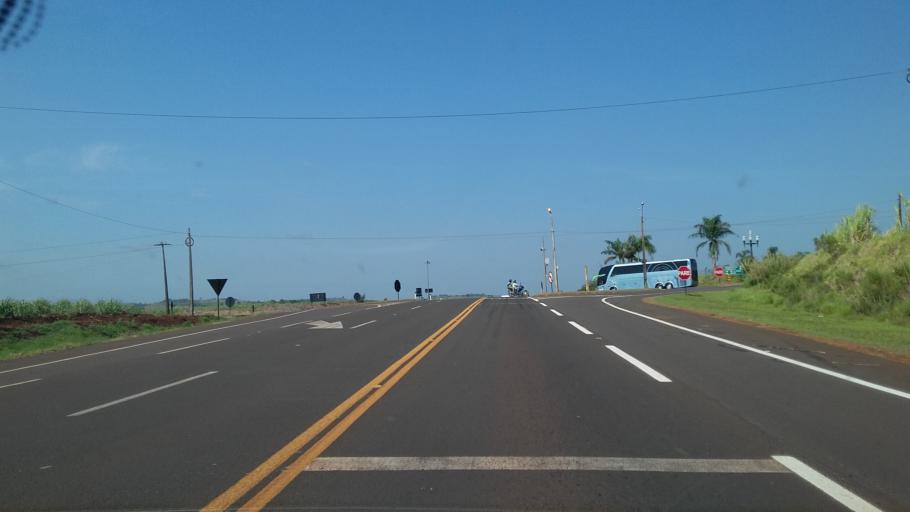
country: BR
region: Parana
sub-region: Bandeirantes
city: Bandeirantes
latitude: -23.1244
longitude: -50.3574
